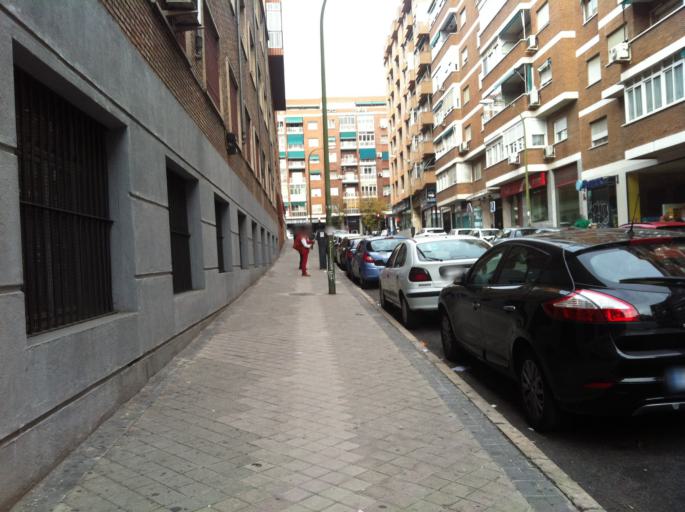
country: ES
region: Madrid
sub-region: Provincia de Madrid
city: Arganzuela
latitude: 40.4058
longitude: -3.6958
